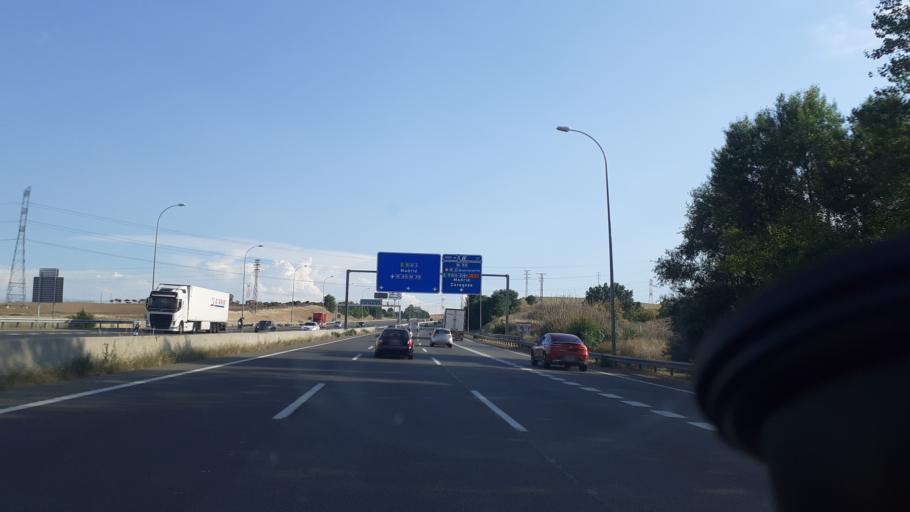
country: ES
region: Madrid
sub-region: Provincia de Madrid
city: San Sebastian de los Reyes
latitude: 40.5740
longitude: -3.5856
